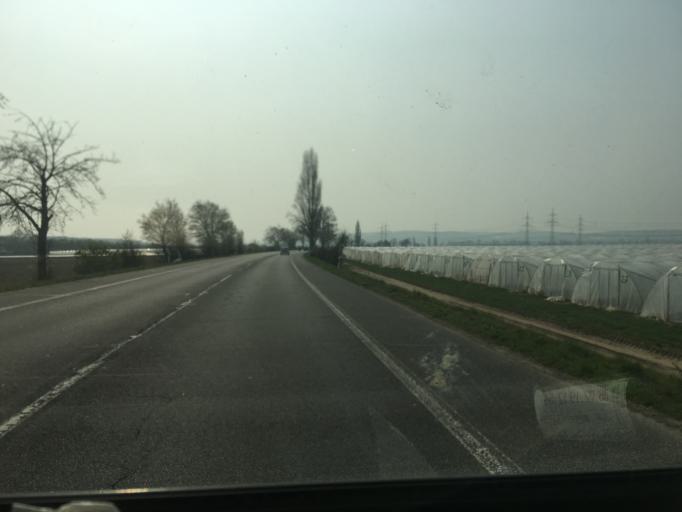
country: DE
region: North Rhine-Westphalia
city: Bornheim
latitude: 50.7917
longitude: 6.9918
